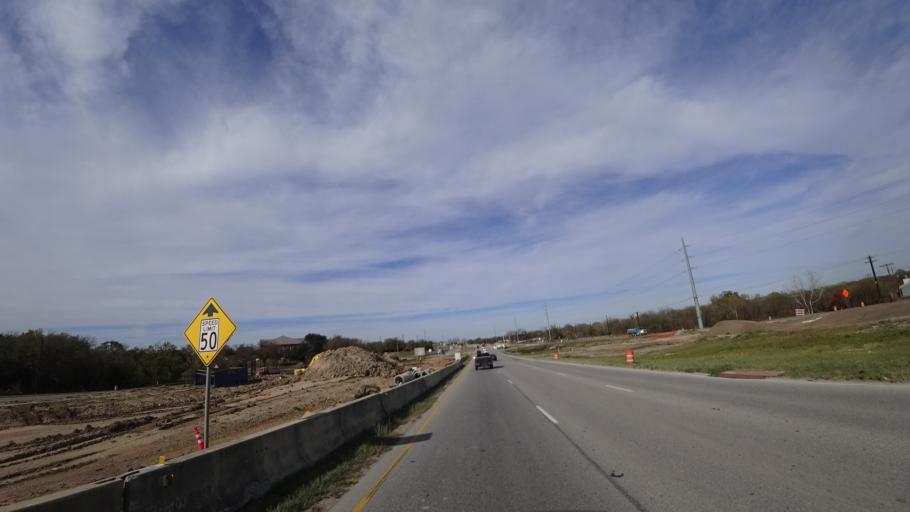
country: US
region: Texas
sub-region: Travis County
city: Austin
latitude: 30.2275
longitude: -97.6823
